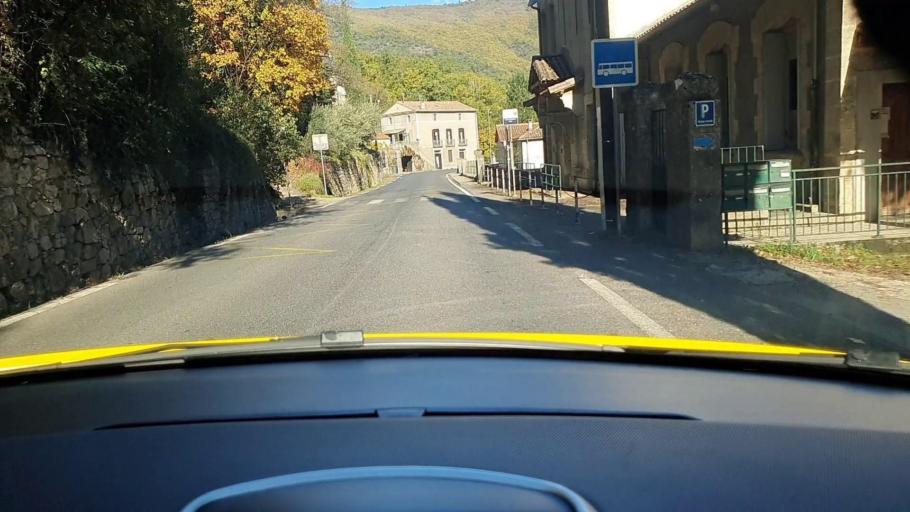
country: FR
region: Languedoc-Roussillon
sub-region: Departement du Gard
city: Aveze
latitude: 43.9711
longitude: 3.5277
